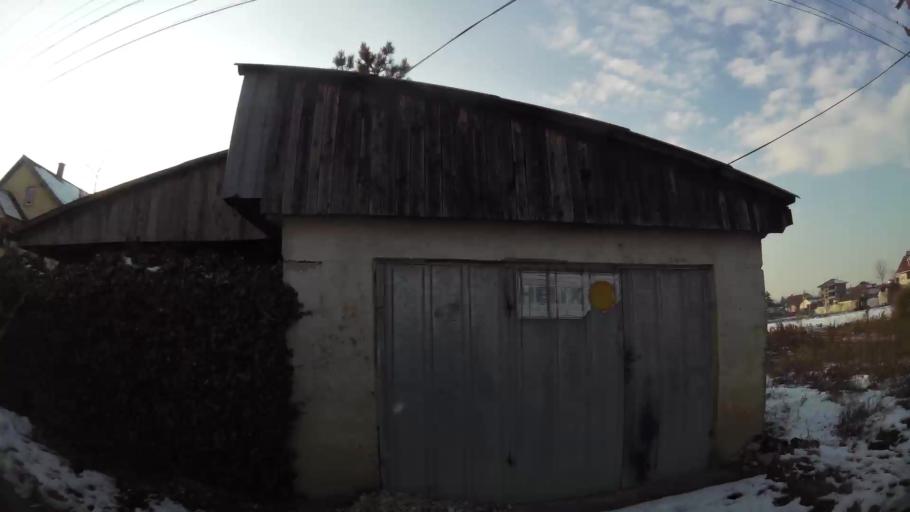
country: MK
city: Creshevo
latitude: 42.0265
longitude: 21.5200
